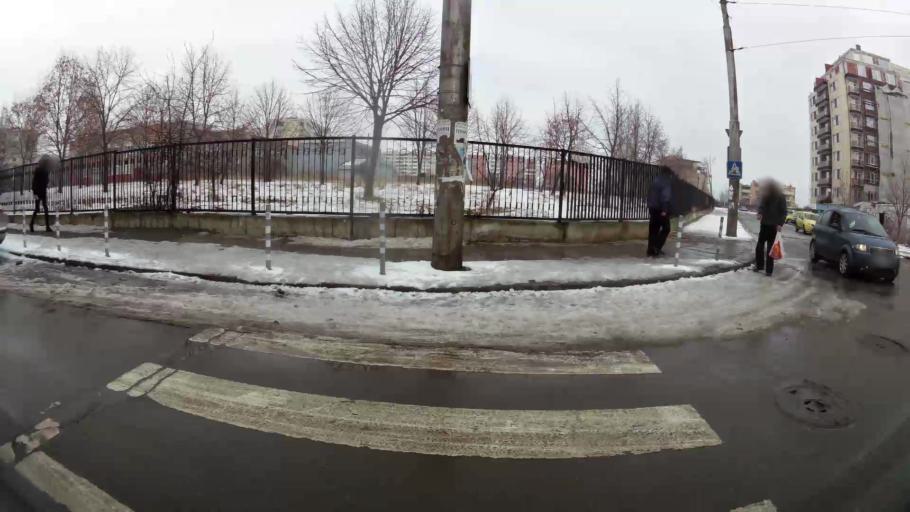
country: BG
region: Sofia-Capital
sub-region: Stolichna Obshtina
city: Sofia
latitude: 42.7131
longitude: 23.3794
